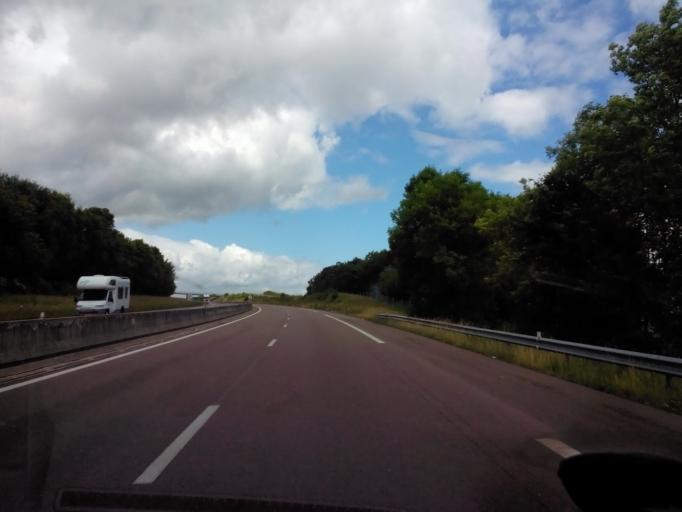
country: FR
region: Lorraine
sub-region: Departement des Vosges
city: Chatenois
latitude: 48.3994
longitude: 5.8810
